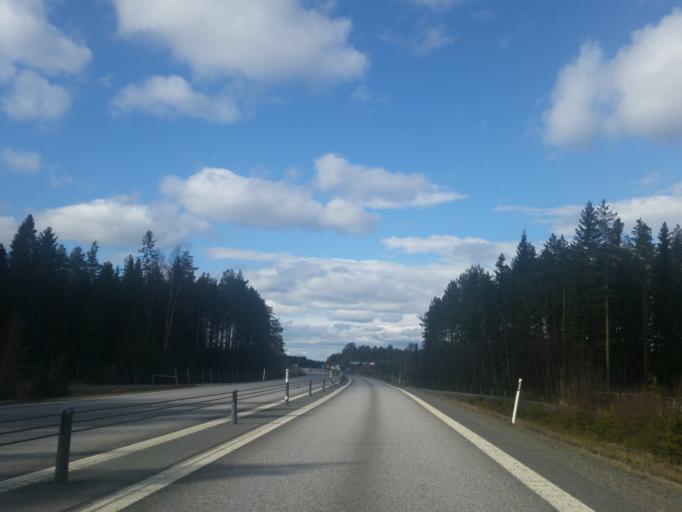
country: SE
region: Vaesterbotten
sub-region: Robertsfors Kommun
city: Robertsfors
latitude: 64.1121
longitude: 20.8799
